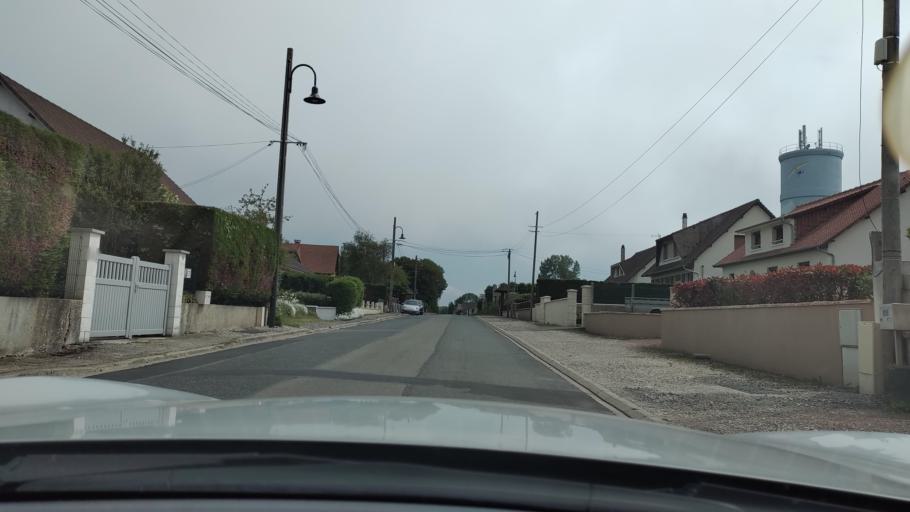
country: FR
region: Picardie
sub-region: Departement de la Somme
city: Ault
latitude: 50.0795
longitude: 1.4557
